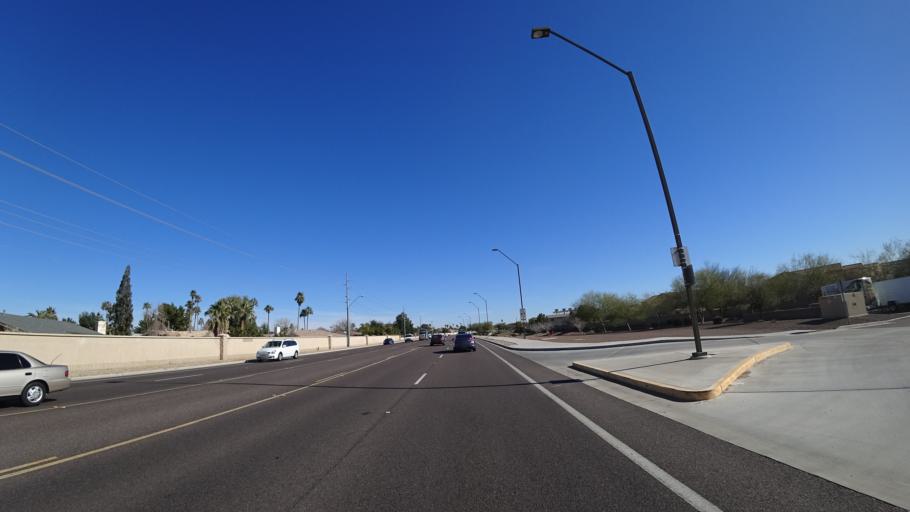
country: US
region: Arizona
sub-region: Maricopa County
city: Litchfield Park
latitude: 33.4902
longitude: -112.3485
